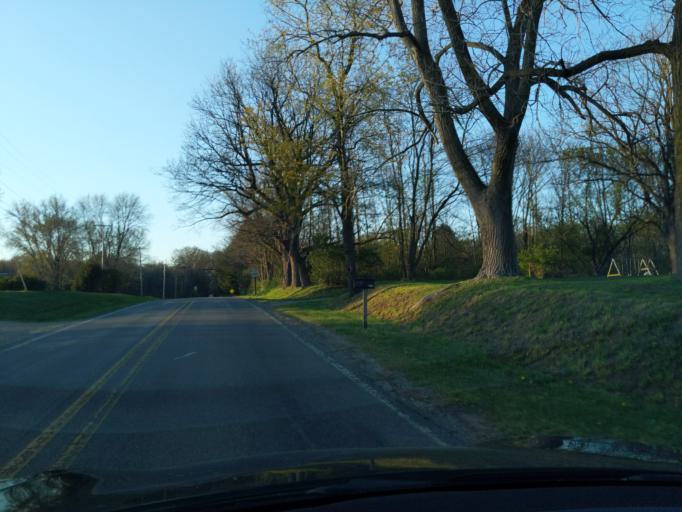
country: US
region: Michigan
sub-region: Jackson County
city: Jackson
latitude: 42.2591
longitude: -84.4832
